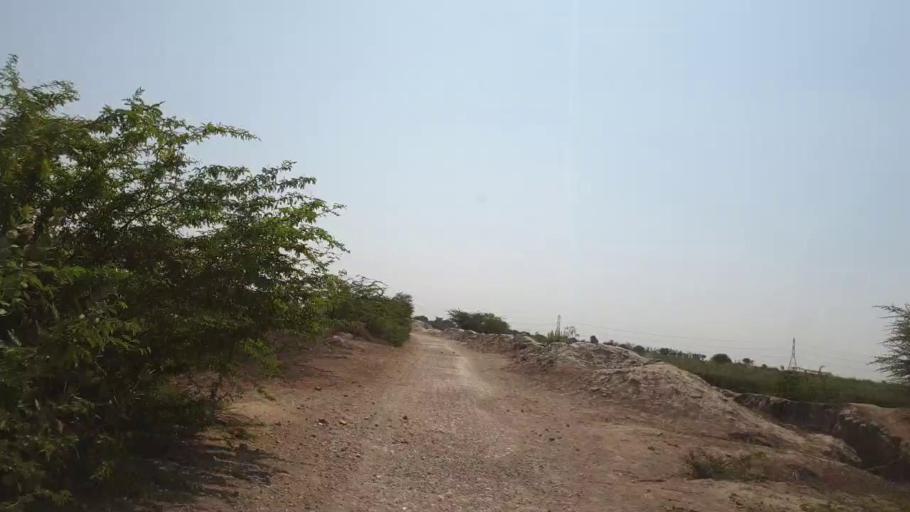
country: PK
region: Sindh
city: Nabisar
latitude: 25.0760
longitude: 69.5339
